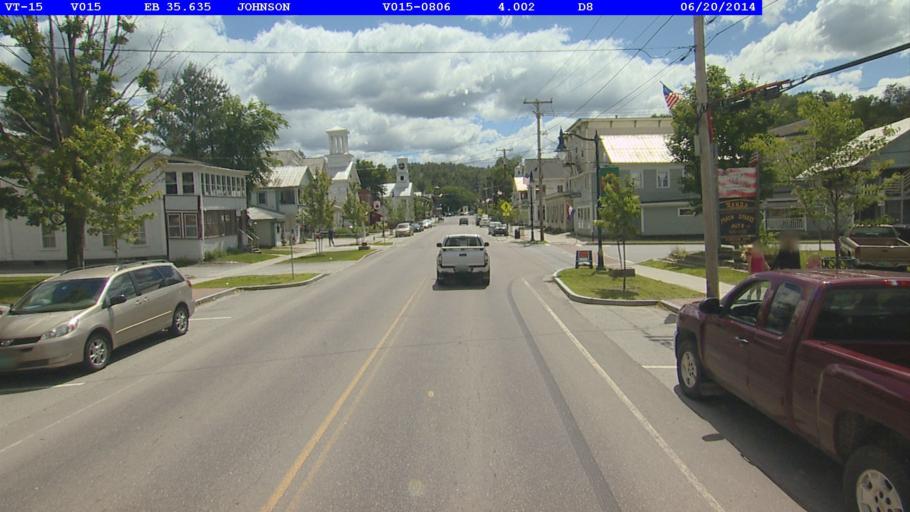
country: US
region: Vermont
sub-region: Lamoille County
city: Johnson
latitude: 44.6358
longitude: -72.6809
